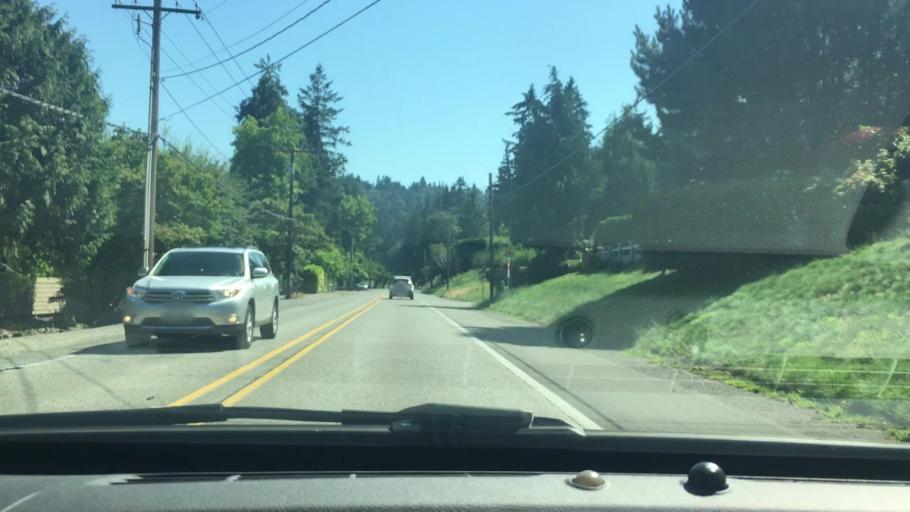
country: US
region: Washington
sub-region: King County
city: West Lake Sammamish
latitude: 47.5840
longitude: -122.1115
